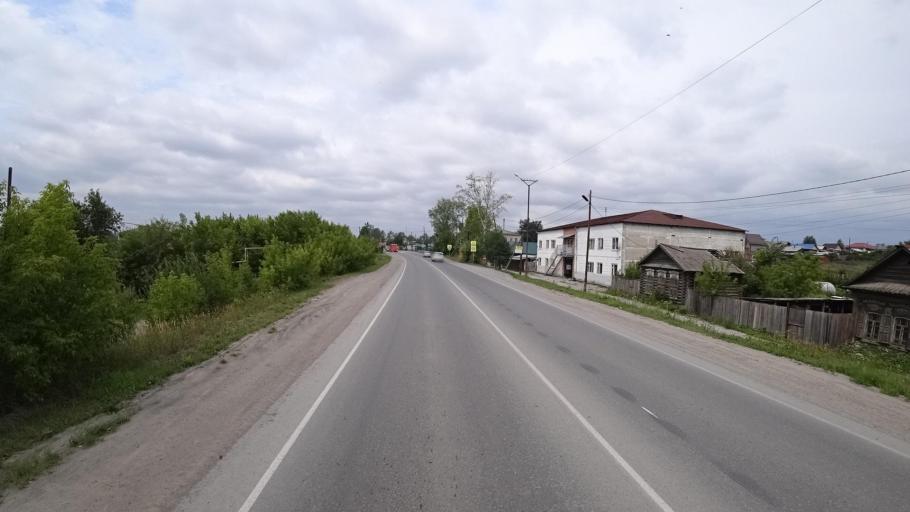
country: RU
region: Sverdlovsk
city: Kamyshlov
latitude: 56.8464
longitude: 62.6839
